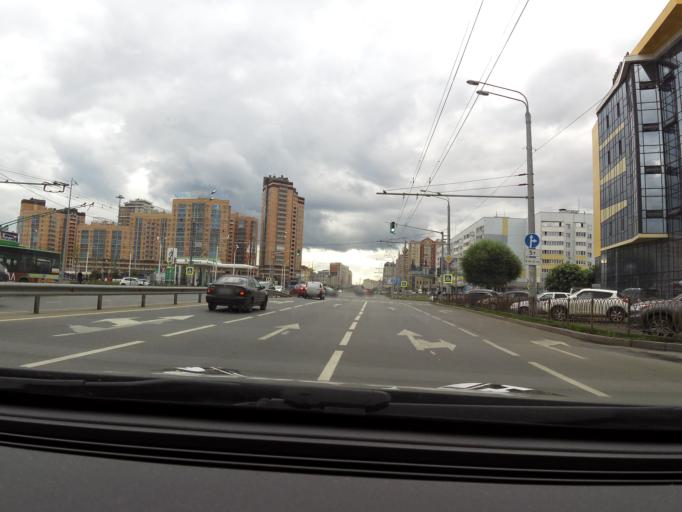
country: RU
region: Tatarstan
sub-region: Gorod Kazan'
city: Kazan
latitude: 55.8195
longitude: 49.1278
